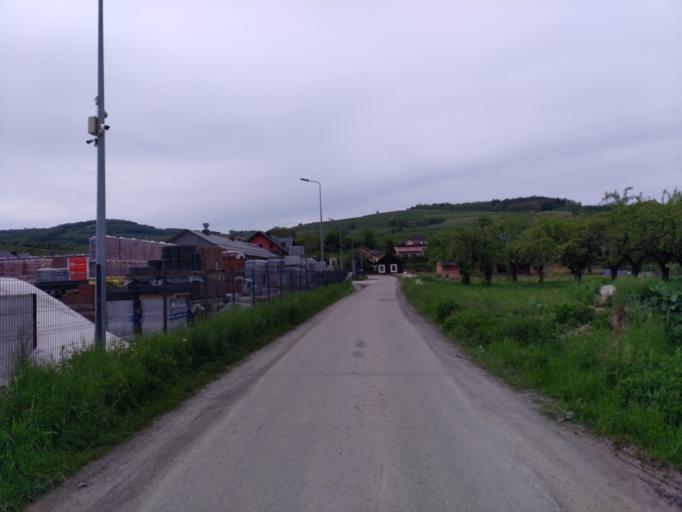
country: PL
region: Lesser Poland Voivodeship
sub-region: Powiat nowosadecki
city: Lacko
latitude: 49.5524
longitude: 20.4292
